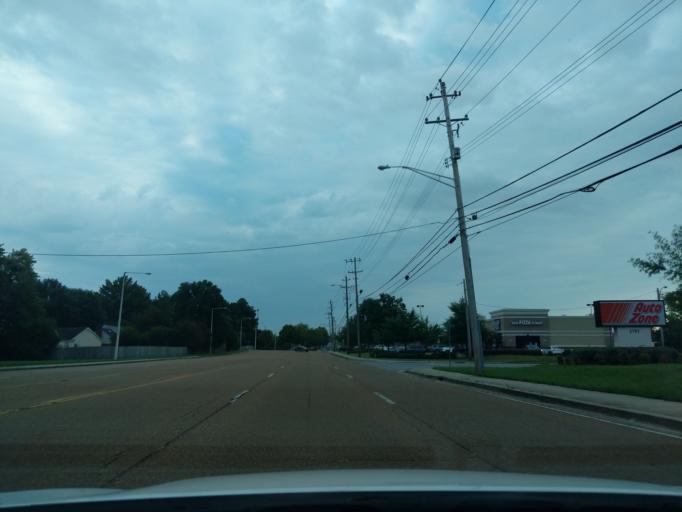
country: US
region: Tennessee
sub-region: Shelby County
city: Germantown
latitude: 35.0734
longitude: -89.8425
